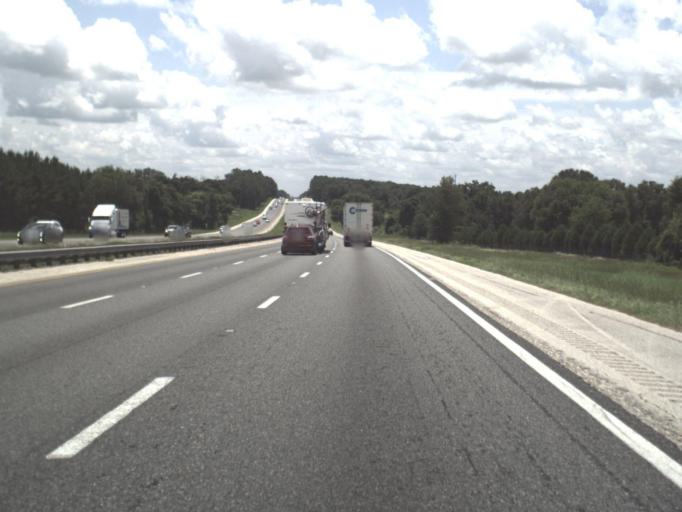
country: US
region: Florida
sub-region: Alachua County
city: High Springs
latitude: 29.8580
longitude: -82.5389
